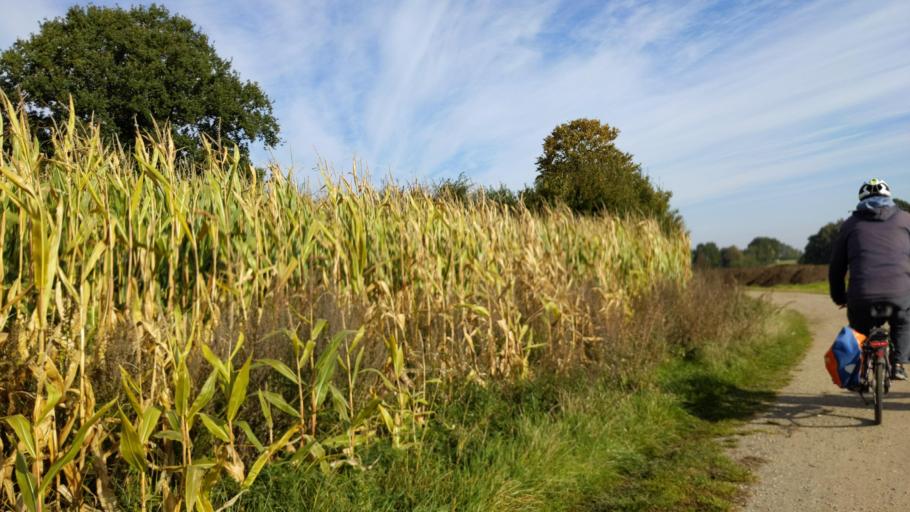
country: DE
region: Schleswig-Holstein
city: Zarpen
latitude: 53.8607
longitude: 10.5128
